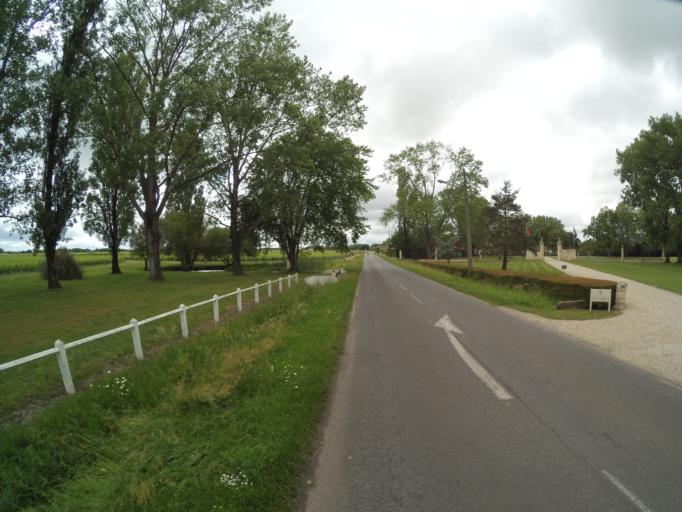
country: FR
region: Aquitaine
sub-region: Departement de la Gironde
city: Macau
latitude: 45.0210
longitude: -0.6317
